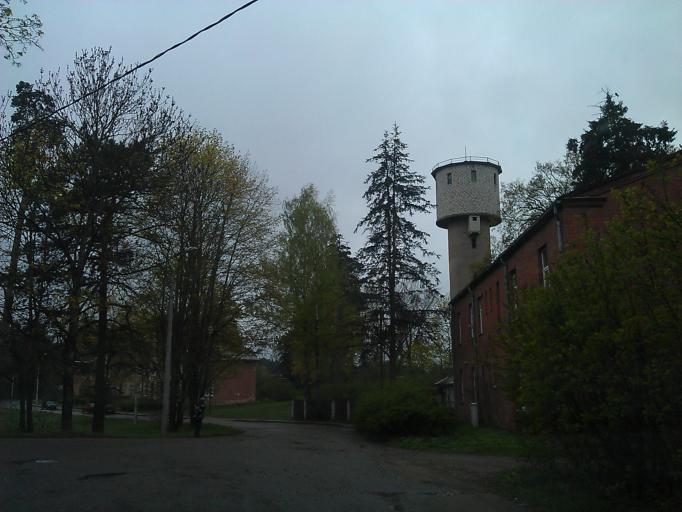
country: LV
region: Riga
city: Bergi
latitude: 56.9625
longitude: 24.3008
